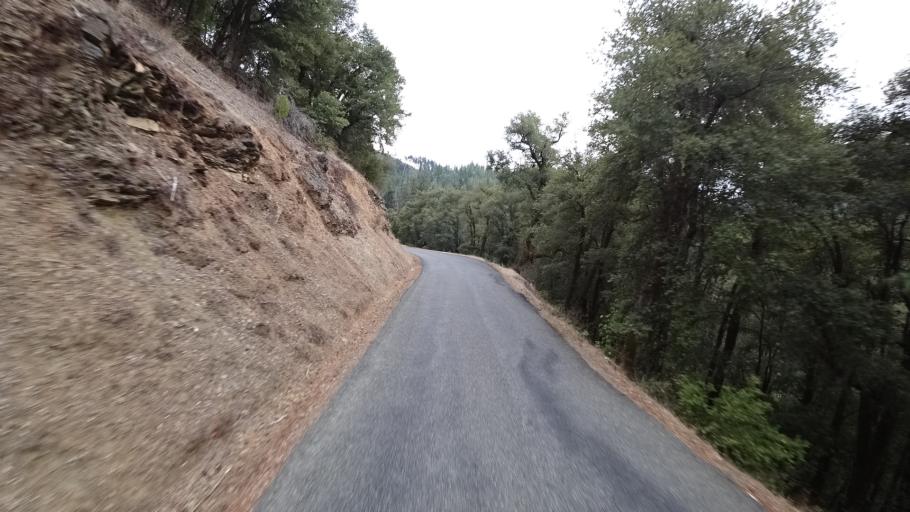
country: US
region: California
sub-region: Siskiyou County
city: Happy Camp
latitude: 41.7590
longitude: -123.3616
